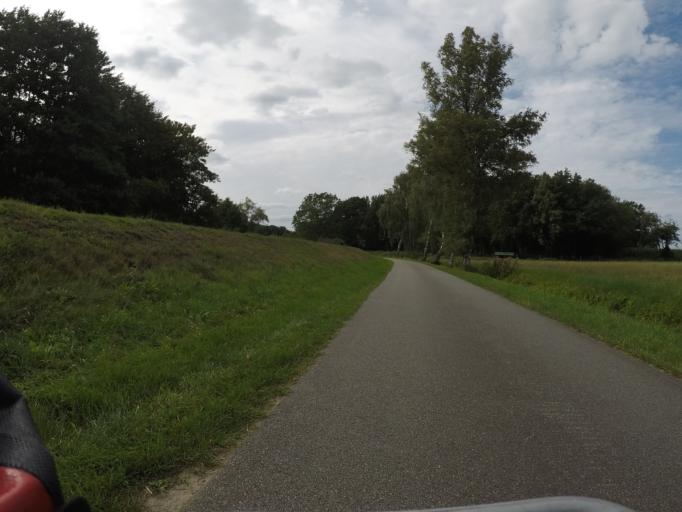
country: DE
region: Lower Saxony
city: Barum
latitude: 53.3405
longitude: 10.3982
